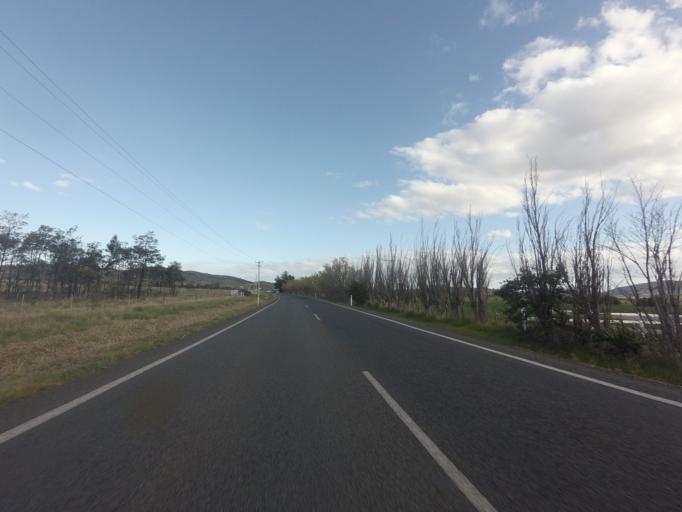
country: AU
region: Tasmania
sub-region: Sorell
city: Sorell
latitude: -42.7431
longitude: 147.5342
